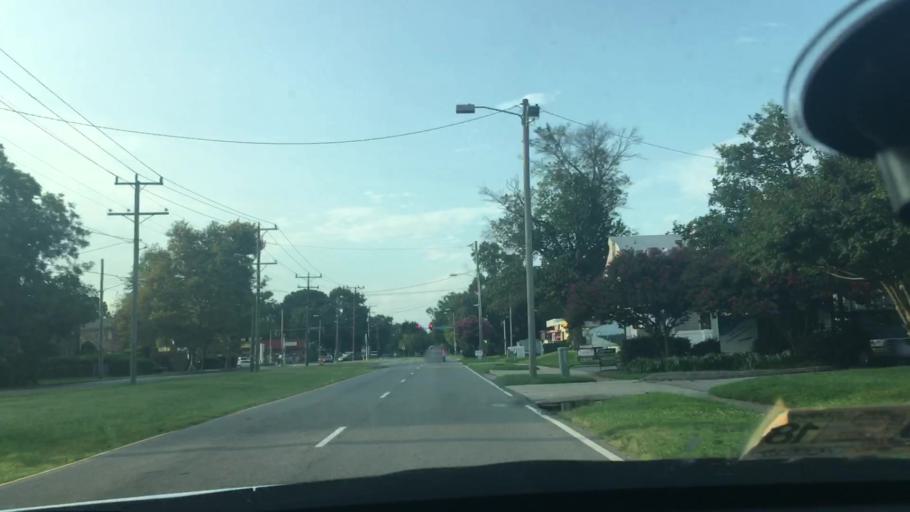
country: US
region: Virginia
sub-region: City of Norfolk
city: Norfolk
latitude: 36.9324
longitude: -76.2441
